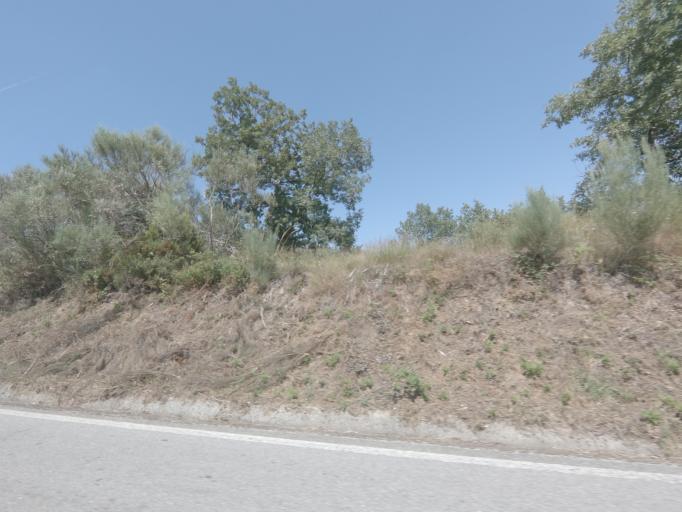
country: PT
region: Viseu
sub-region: Tarouca
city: Tarouca
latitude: 40.9891
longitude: -7.8342
